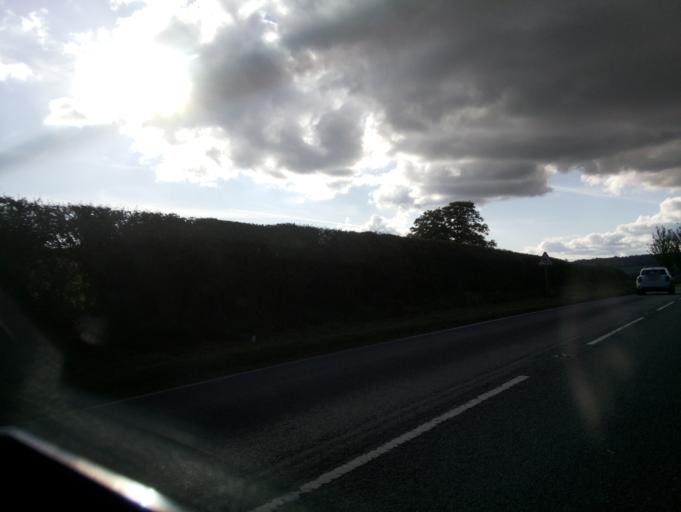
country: GB
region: Wales
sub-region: Sir Powys
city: Hay
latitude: 52.0683
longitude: -3.1431
